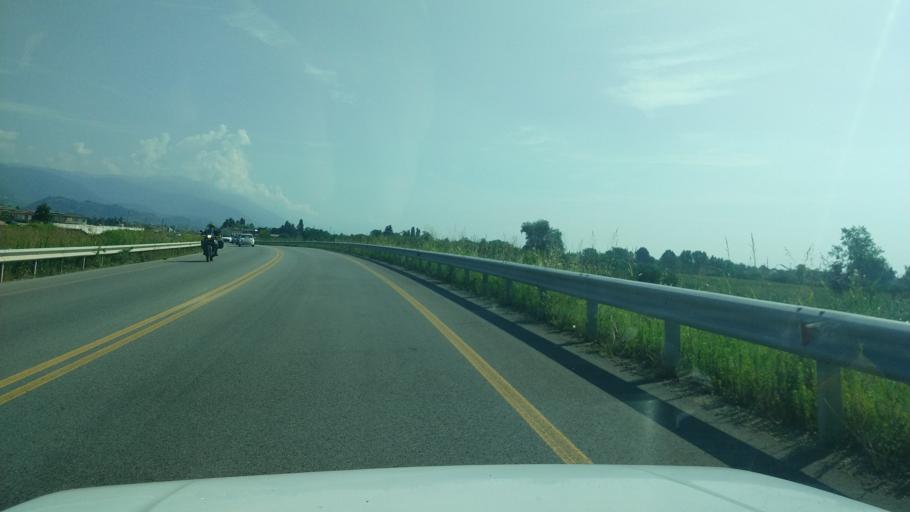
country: IT
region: Veneto
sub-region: Provincia di Vicenza
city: Schiavon
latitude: 45.7114
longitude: 11.6325
